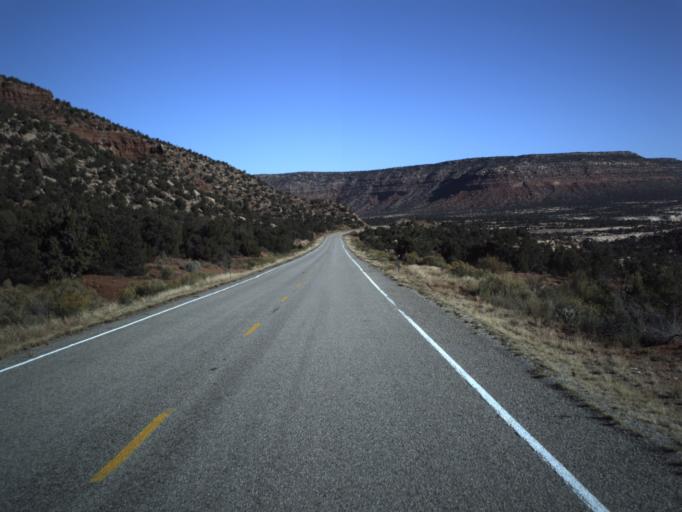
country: US
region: Utah
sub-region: San Juan County
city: Blanding
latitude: 37.5779
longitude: -110.0386
